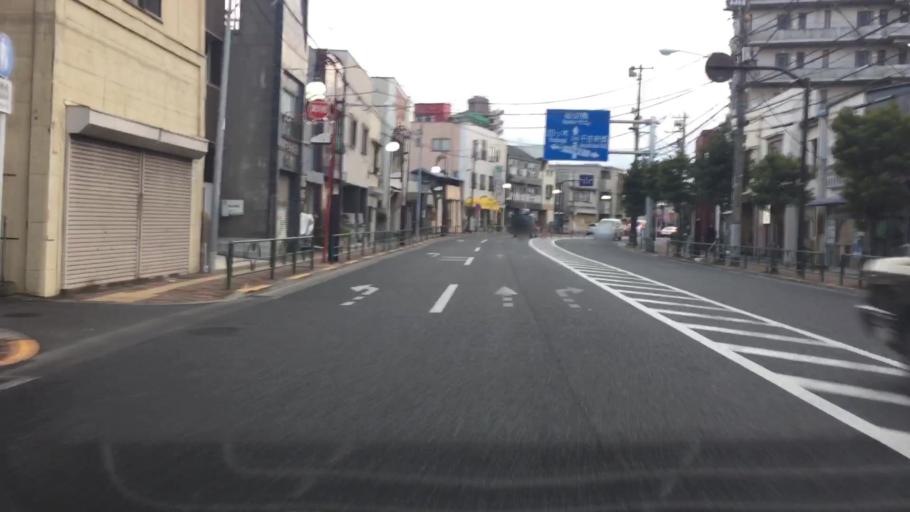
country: JP
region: Saitama
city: Yashio-shi
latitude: 35.7505
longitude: 139.8280
